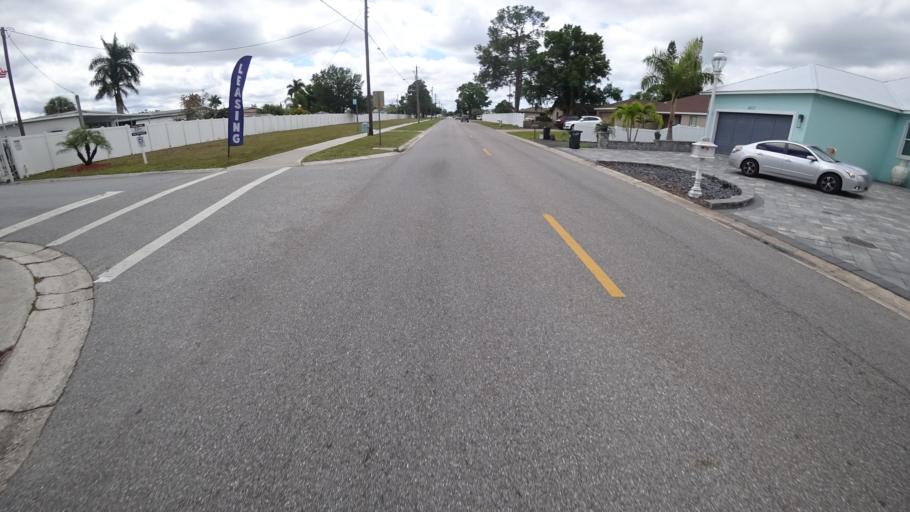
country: US
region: Florida
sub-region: Manatee County
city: South Bradenton
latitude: 27.4562
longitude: -82.5671
